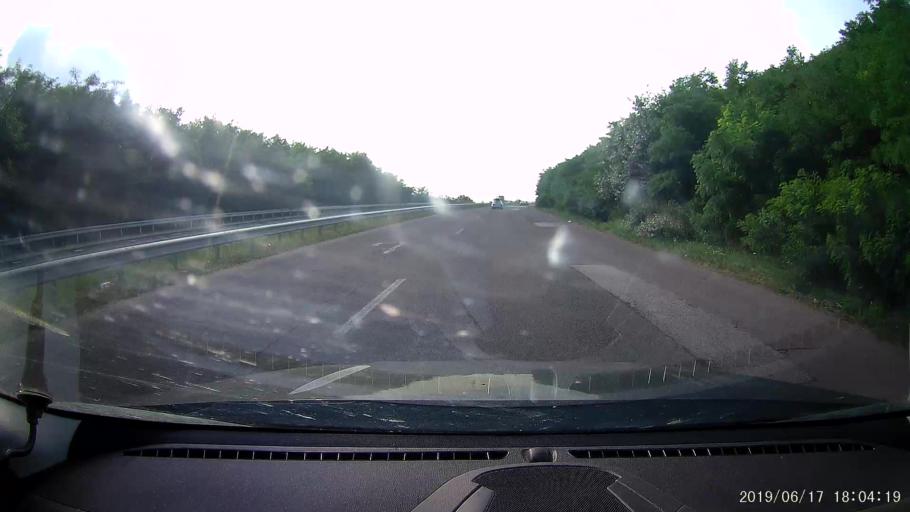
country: BG
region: Khaskovo
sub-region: Obshtina Svilengrad
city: Svilengrad
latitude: 41.7851
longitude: 26.1991
